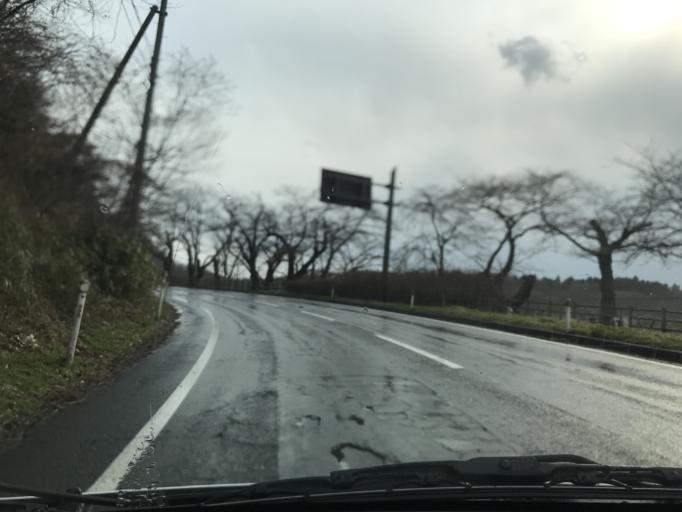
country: JP
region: Iwate
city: Kitakami
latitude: 39.2705
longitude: 141.1254
